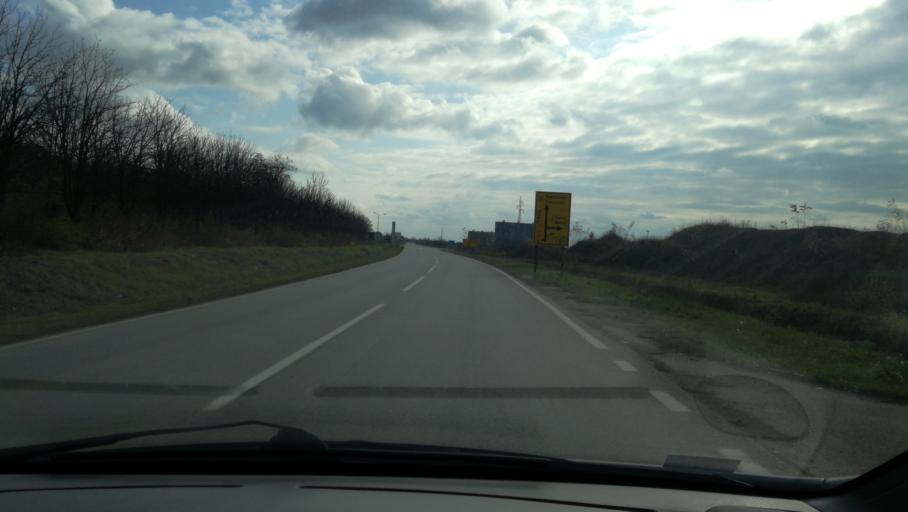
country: RS
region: Autonomna Pokrajina Vojvodina
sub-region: Severnobanatski Okrug
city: Kikinda
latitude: 45.8083
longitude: 20.4330
